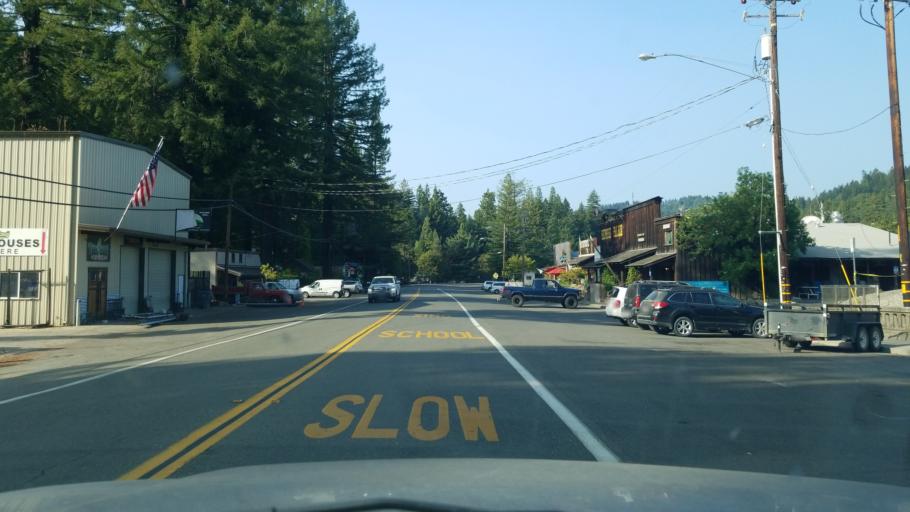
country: US
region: California
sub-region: Humboldt County
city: Redway
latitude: 40.2348
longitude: -123.8244
